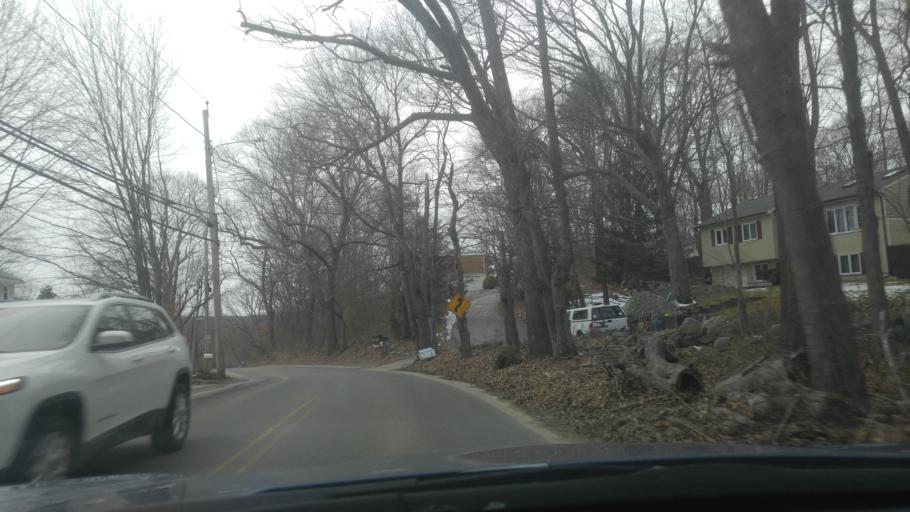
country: US
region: Rhode Island
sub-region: Kent County
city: West Warwick
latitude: 41.6783
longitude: -71.5206
